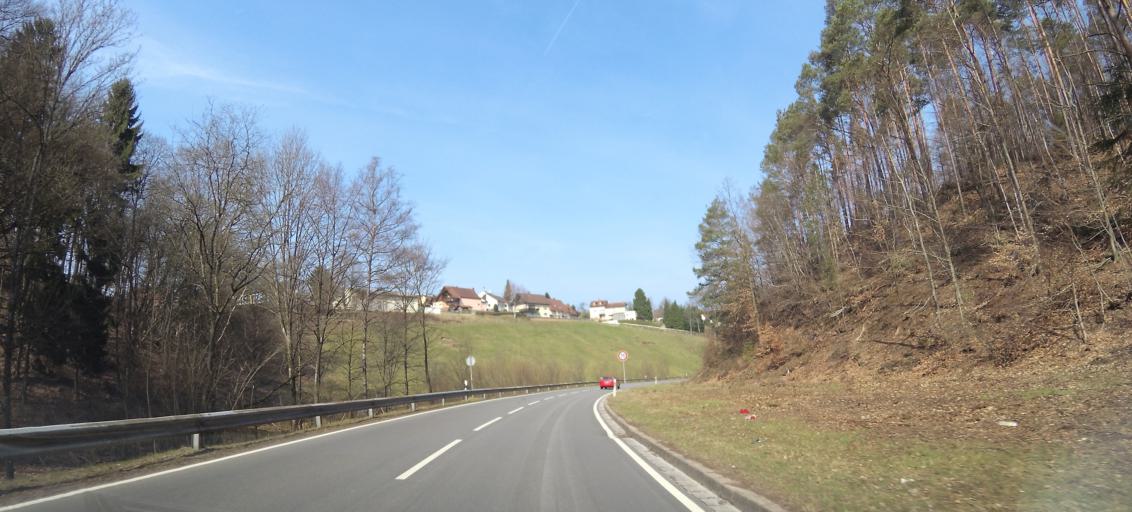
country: DE
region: Rheinland-Pfalz
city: Stelzenberg
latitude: 49.3787
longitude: 7.7436
